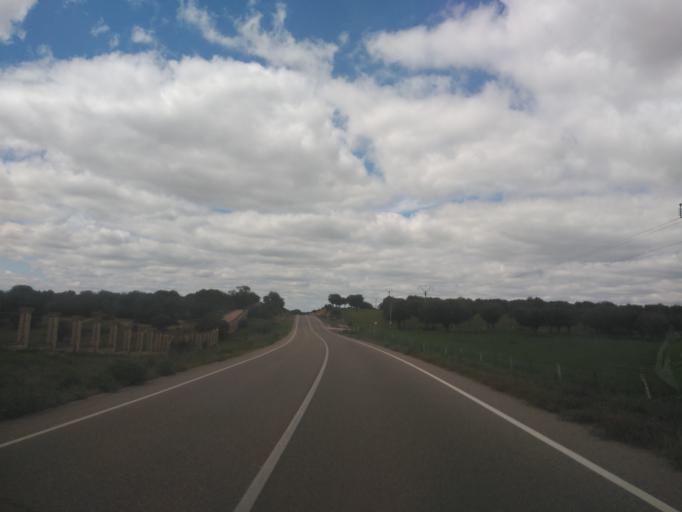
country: ES
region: Castille and Leon
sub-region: Provincia de Salamanca
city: Florida de Liebana
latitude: 41.0375
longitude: -5.7388
